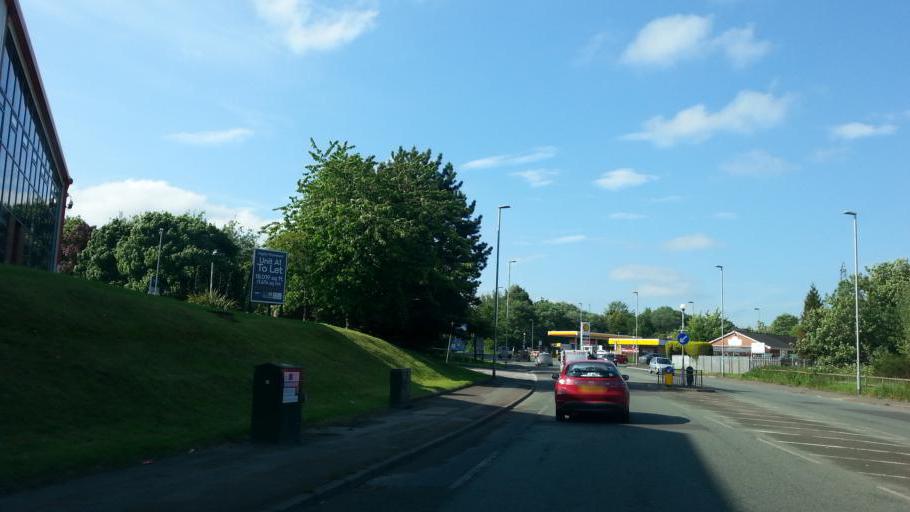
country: GB
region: England
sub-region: Borough of Rochdale
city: Middleton
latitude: 53.5401
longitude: -2.1745
